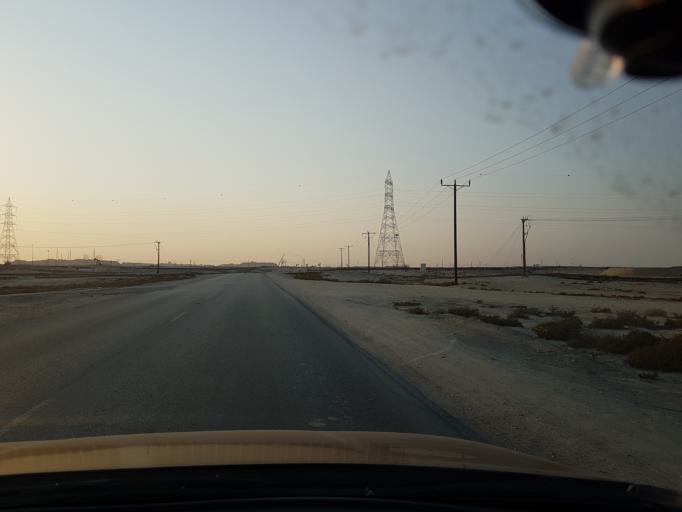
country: BH
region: Central Governorate
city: Dar Kulayb
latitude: 26.0174
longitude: 50.5750
